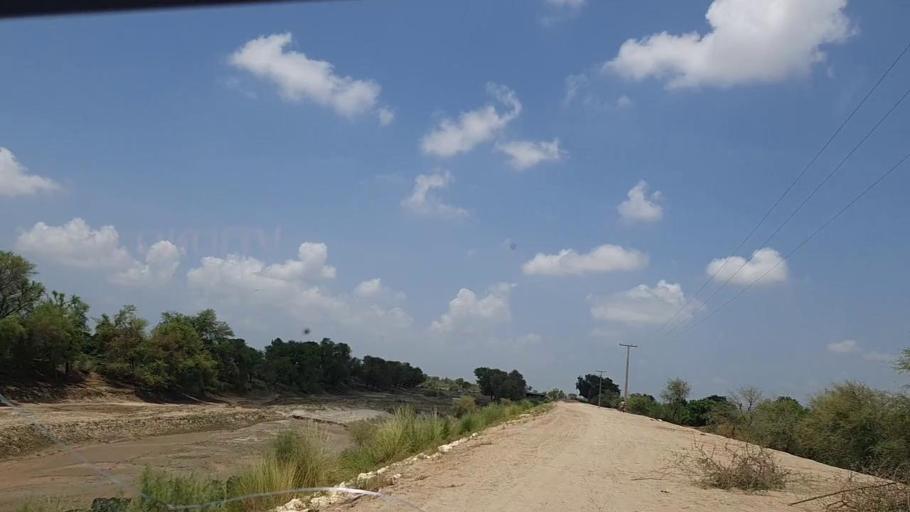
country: PK
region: Sindh
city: Tharu Shah
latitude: 26.9261
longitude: 67.9899
